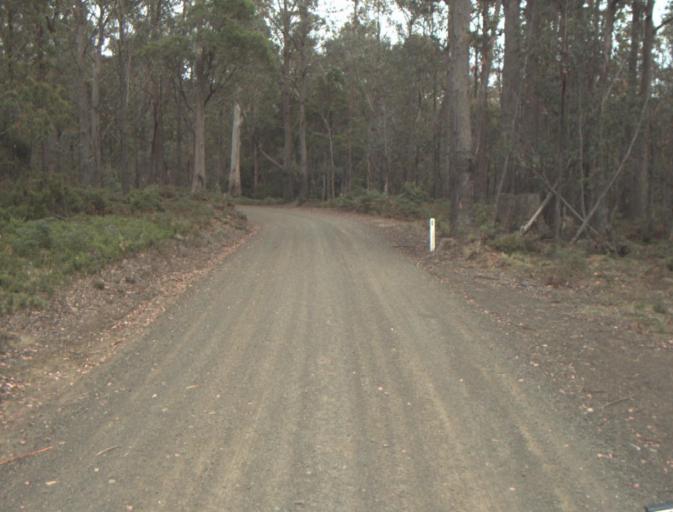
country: AU
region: Tasmania
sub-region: Dorset
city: Scottsdale
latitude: -41.4982
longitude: 147.6033
